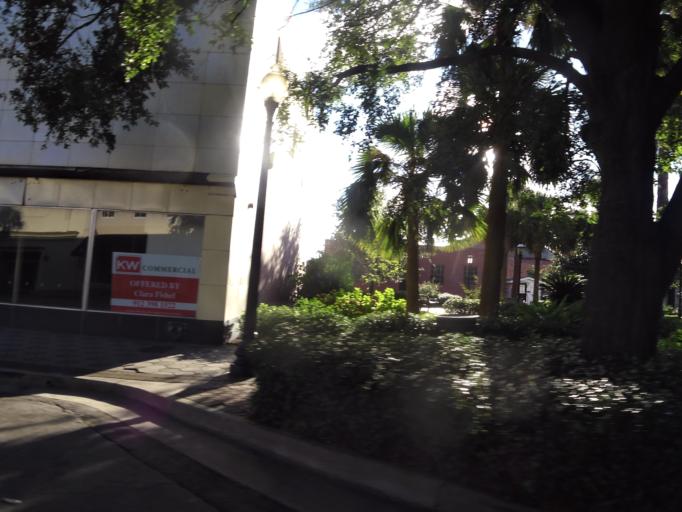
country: US
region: Georgia
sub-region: Glynn County
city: Brunswick
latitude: 31.1497
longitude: -81.4957
